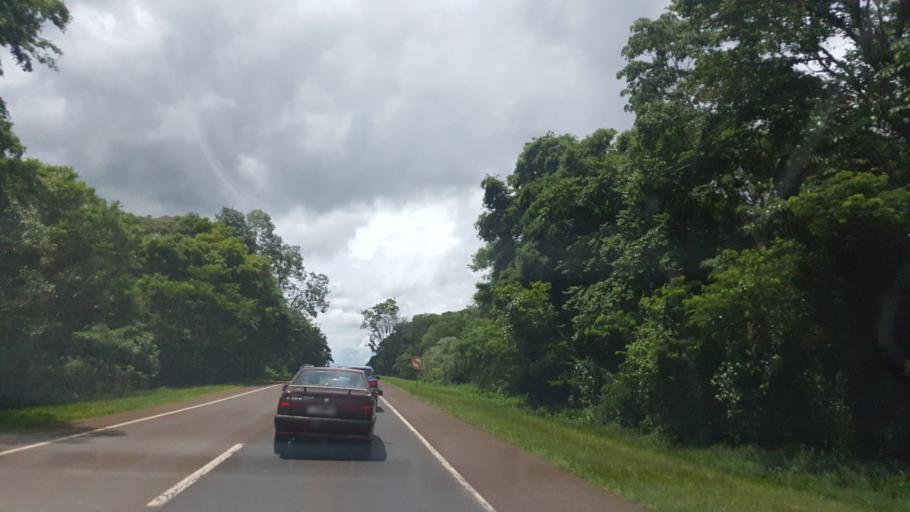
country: AR
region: Misiones
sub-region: Departamento de Iguazu
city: Puerto Iguazu
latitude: -25.6988
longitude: -54.5148
